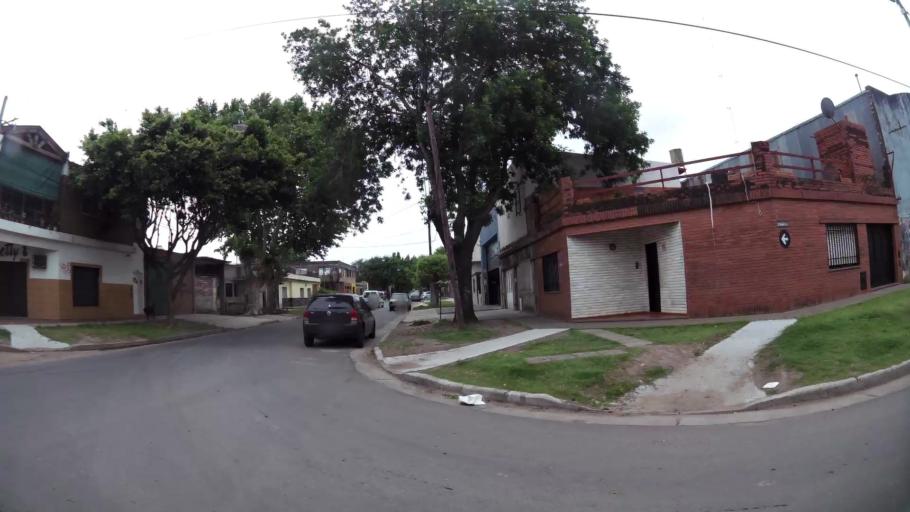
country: AR
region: Santa Fe
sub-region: Departamento de Rosario
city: Rosario
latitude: -32.9874
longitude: -60.6601
